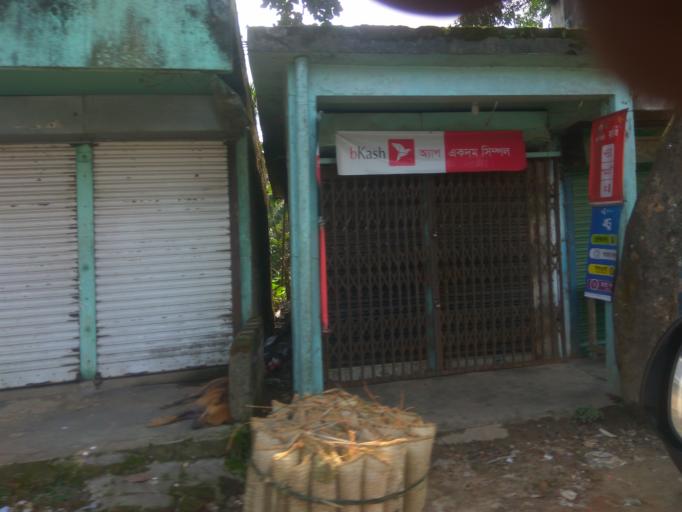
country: IN
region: Assam
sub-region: Karimganj
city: Karimganj
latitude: 24.8097
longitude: 92.1829
